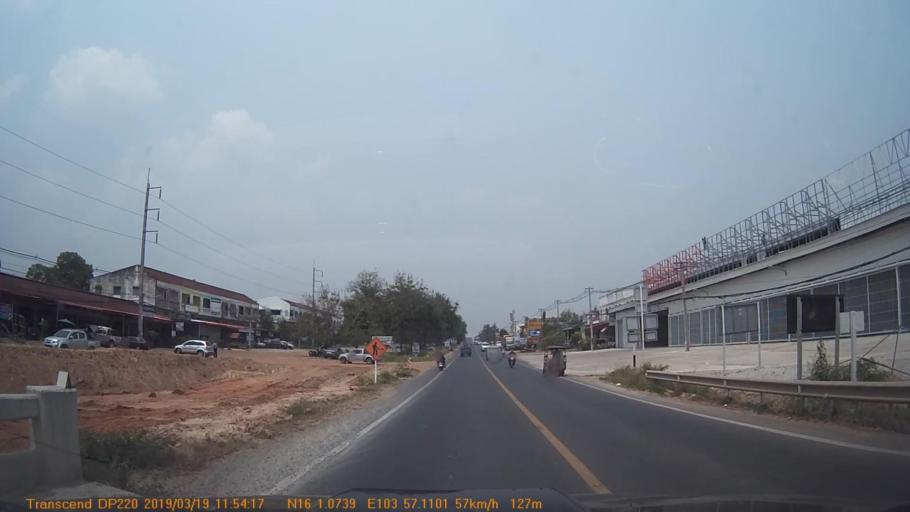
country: TH
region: Roi Et
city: Ban Selaphum
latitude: 16.0180
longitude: 103.9517
